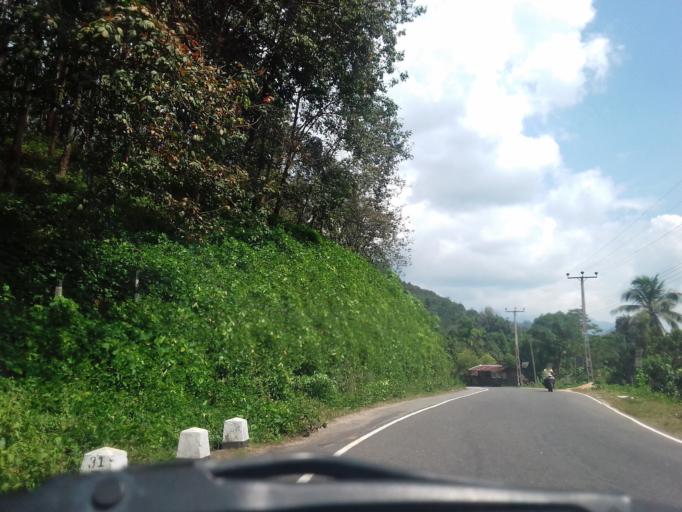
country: LK
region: Central
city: Hatton
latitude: 6.9963
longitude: 80.3518
